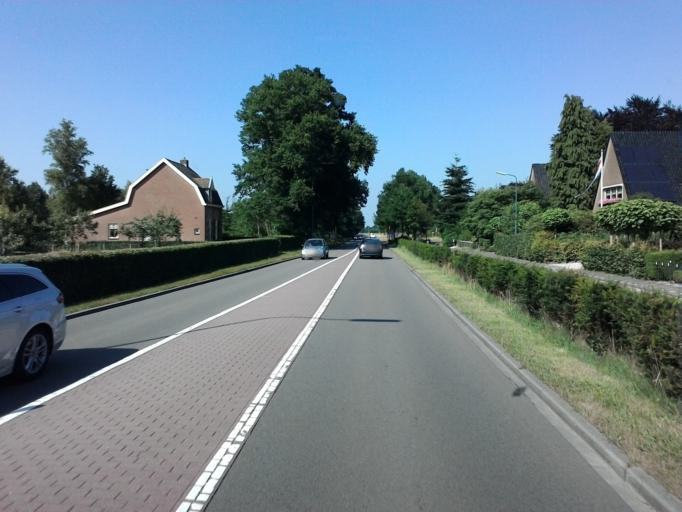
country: NL
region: Utrecht
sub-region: Gemeente Utrechtse Heuvelrug
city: Maarsbergen
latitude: 52.0614
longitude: 5.4048
